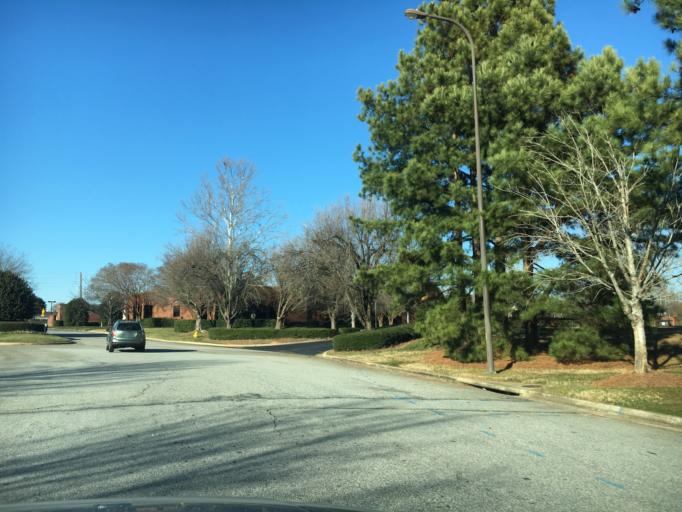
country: US
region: South Carolina
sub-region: Greenville County
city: Mauldin
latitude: 34.8097
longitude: -82.2779
